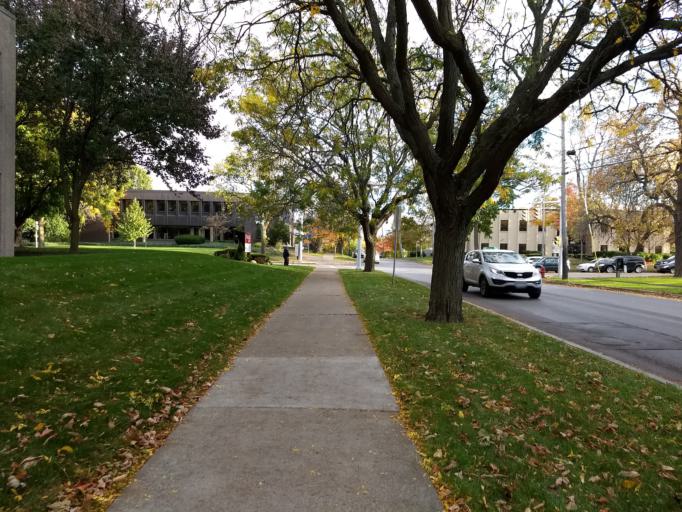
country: US
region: New York
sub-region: Onondaga County
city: Syracuse
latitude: 43.0596
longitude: -76.1348
